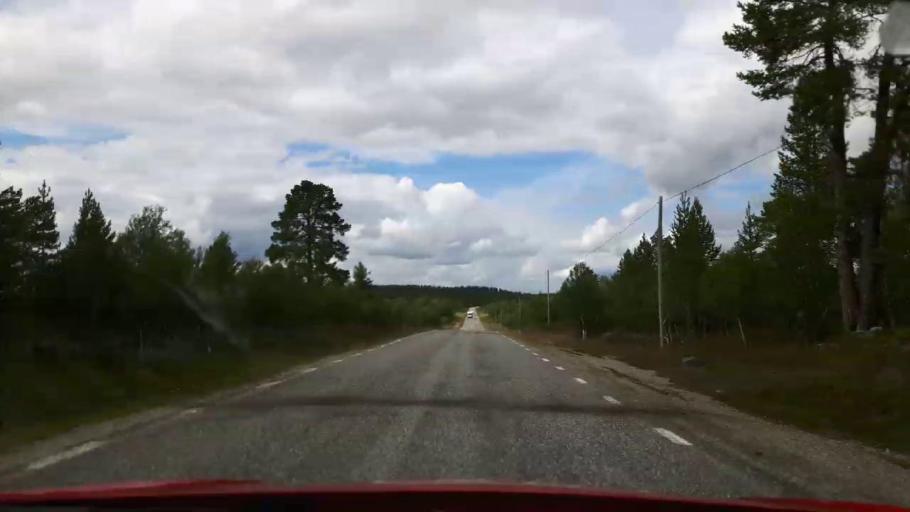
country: NO
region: Hedmark
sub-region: Engerdal
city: Engerdal
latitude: 62.2917
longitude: 12.8162
